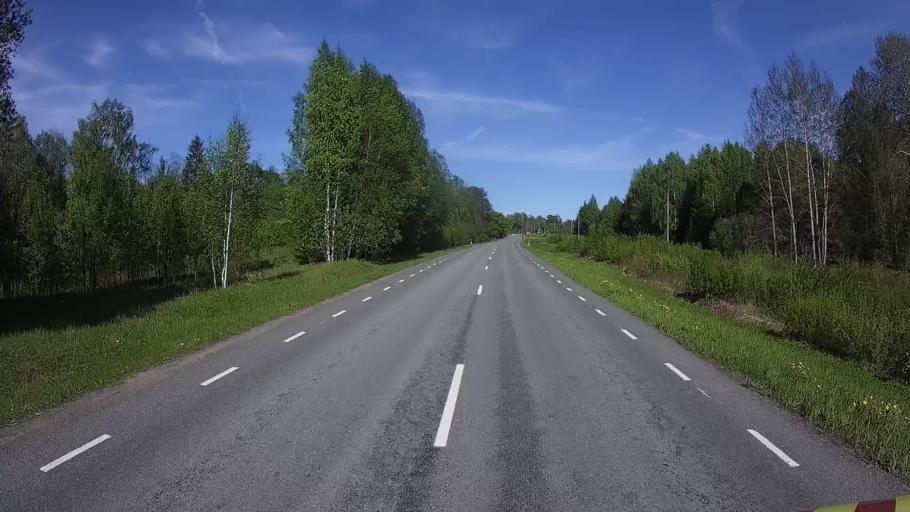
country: EE
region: Vorumaa
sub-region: Antsla vald
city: Vana-Antsla
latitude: 57.9493
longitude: 26.4191
